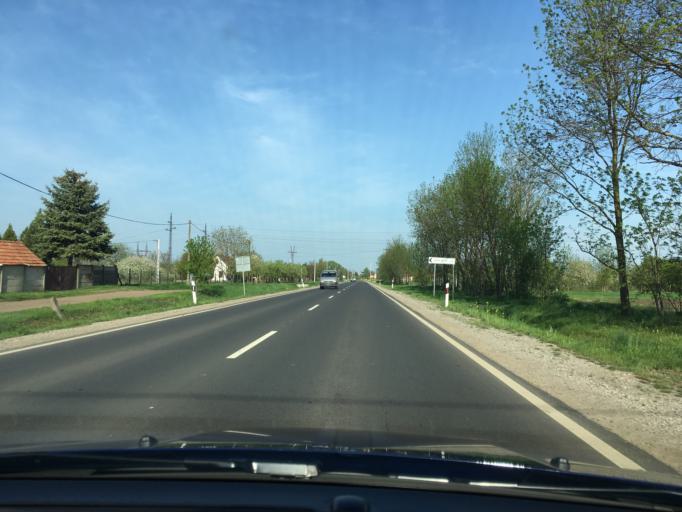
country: HU
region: Bekes
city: Bekescsaba
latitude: 46.6796
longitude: 21.0404
